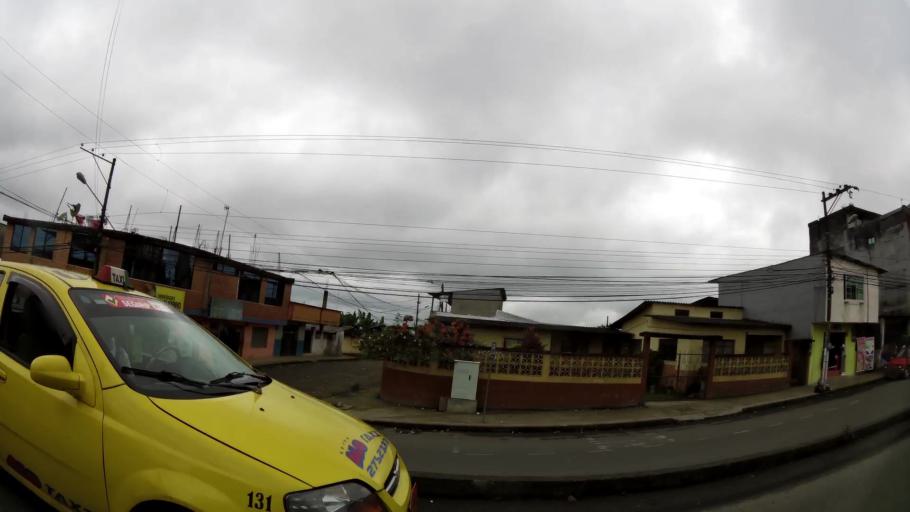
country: EC
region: Santo Domingo de los Tsachilas
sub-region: Canton Santo Domingo de los Colorados
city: Santo Domingo de los Colorados
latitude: -0.2475
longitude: -79.1979
